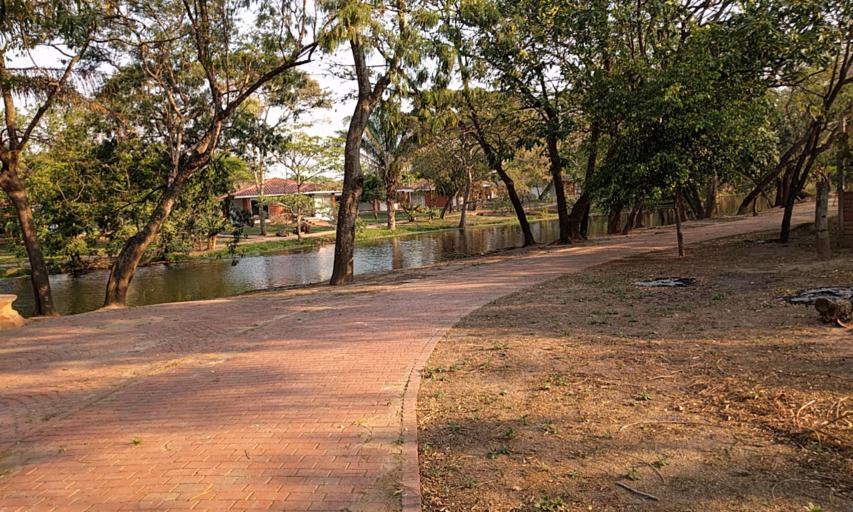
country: BO
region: Santa Cruz
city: Warnes
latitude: -17.4462
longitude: -63.1847
